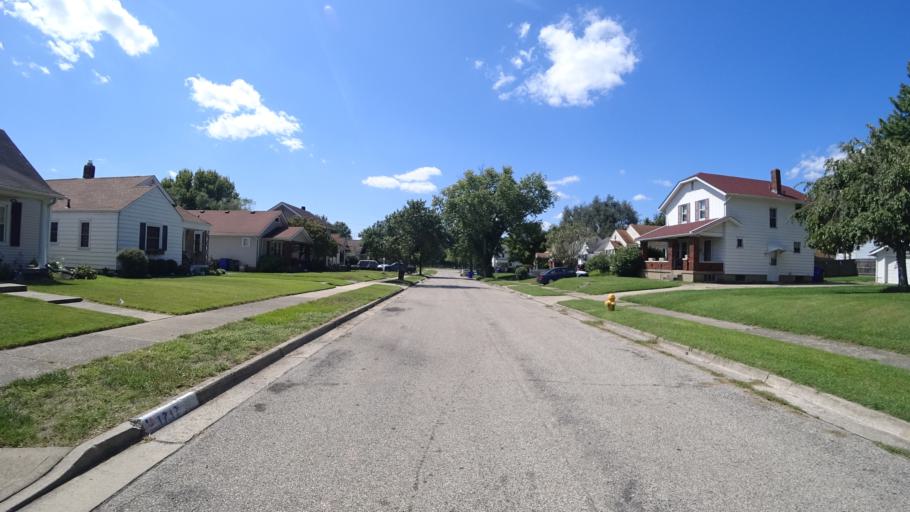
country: US
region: Ohio
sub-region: Butler County
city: Hamilton
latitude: 39.4078
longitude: -84.5367
